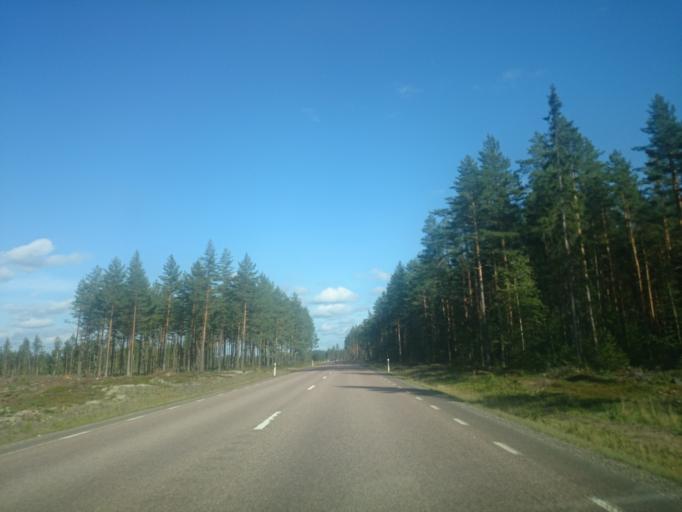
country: SE
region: Gaevleborg
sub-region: Ljusdals Kommun
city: Ljusdal
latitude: 61.8143
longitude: 15.9702
